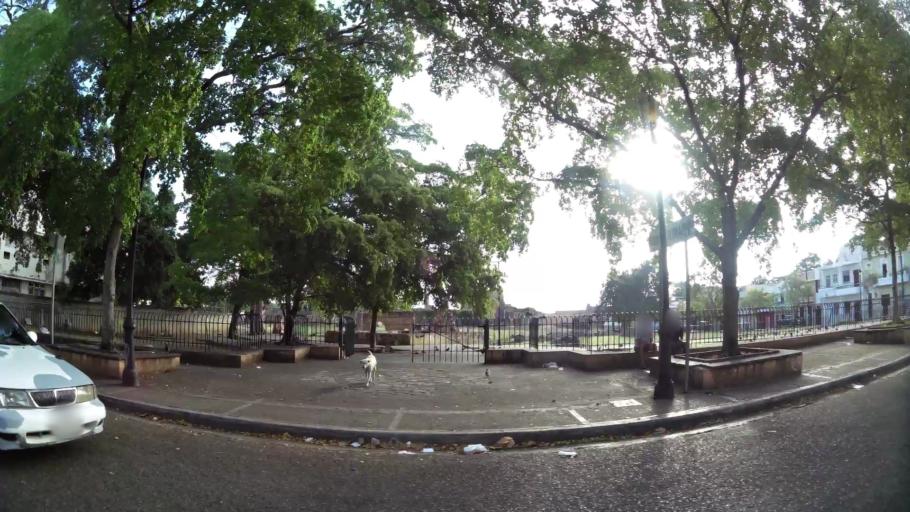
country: DO
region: Nacional
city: San Carlos
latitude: 18.4763
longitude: -69.8869
